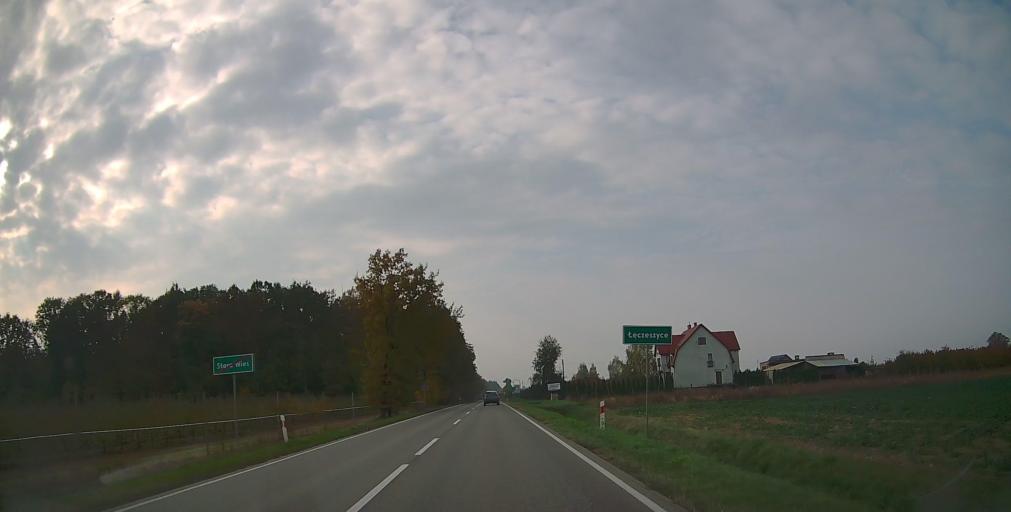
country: PL
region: Masovian Voivodeship
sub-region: Powiat grojecki
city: Belsk Duzy
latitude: 51.7996
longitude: 20.7884
